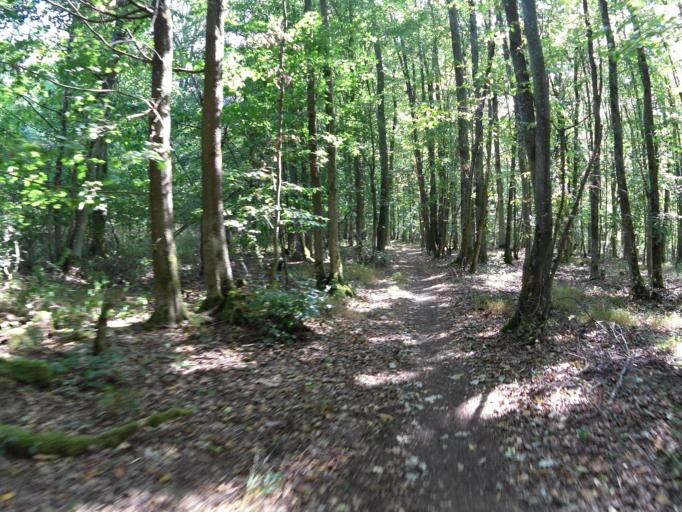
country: DE
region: Bavaria
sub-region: Regierungsbezirk Unterfranken
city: Eisingen
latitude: 49.7711
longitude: 9.8218
